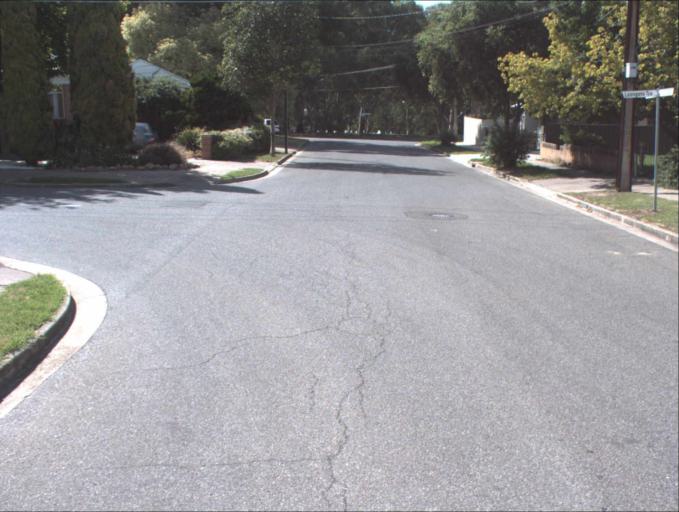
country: AU
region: South Australia
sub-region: Port Adelaide Enfield
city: Gilles Plains
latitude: -34.8652
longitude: 138.6551
